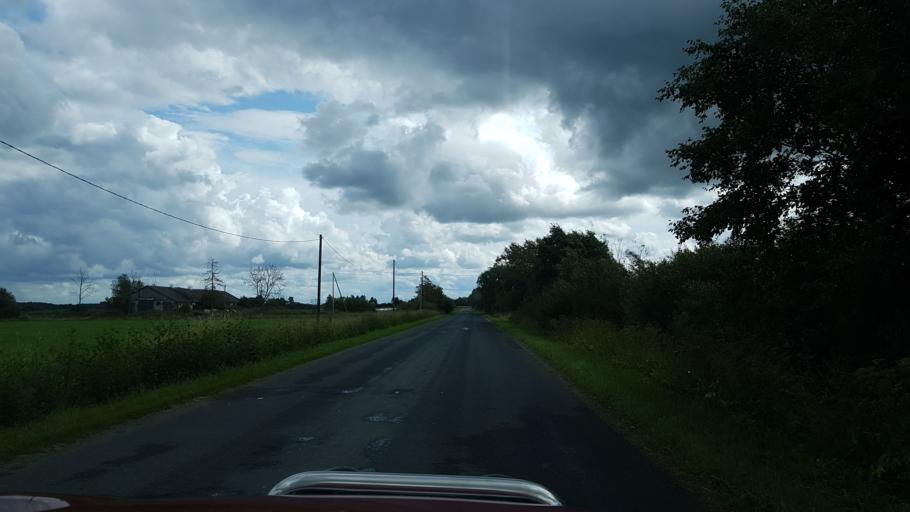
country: EE
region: Laeaene
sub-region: Lihula vald
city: Lihula
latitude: 58.7180
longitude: 23.9858
